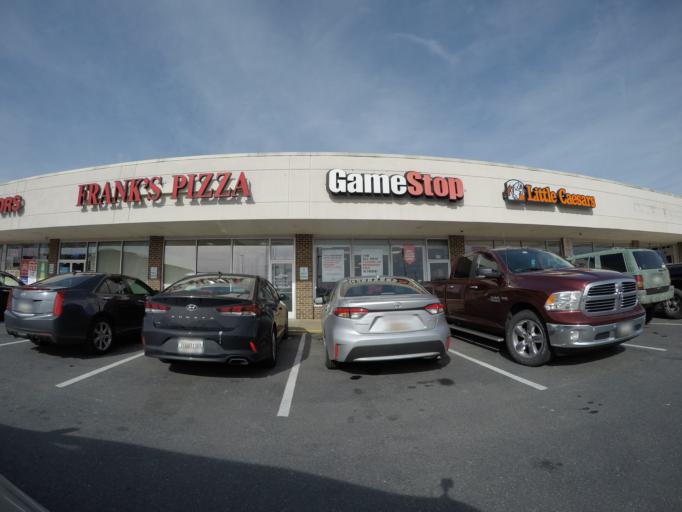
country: US
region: Maryland
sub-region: Cecil County
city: North East
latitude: 39.6112
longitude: -75.9501
